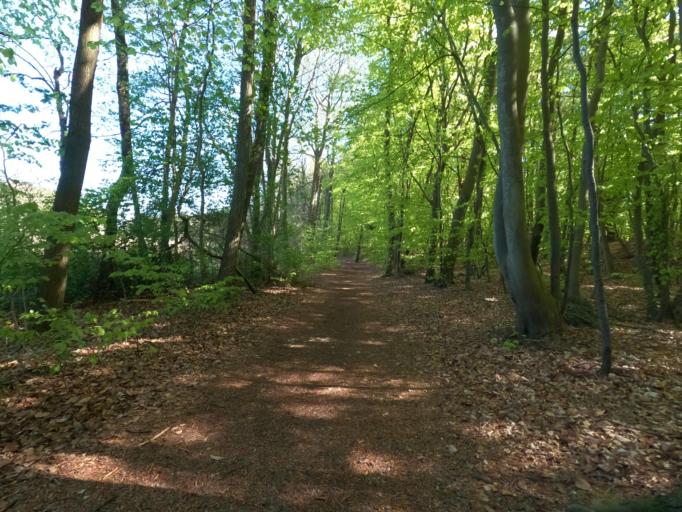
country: DE
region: Mecklenburg-Vorpommern
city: Ostseebad Prerow
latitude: 54.4512
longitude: 12.5593
